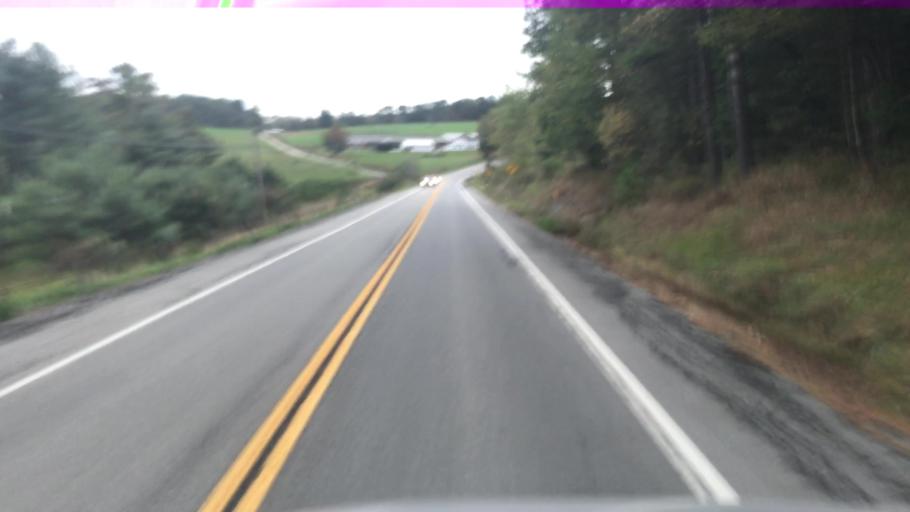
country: US
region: New York
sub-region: Otsego County
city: West End
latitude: 42.5320
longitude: -75.1793
